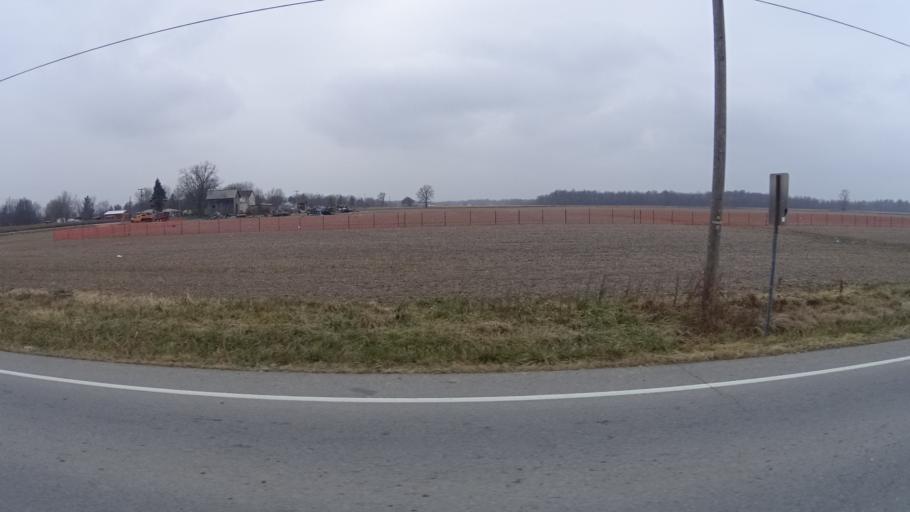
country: US
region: Ohio
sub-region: Lorain County
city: Oberlin
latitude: 41.3384
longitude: -82.1960
